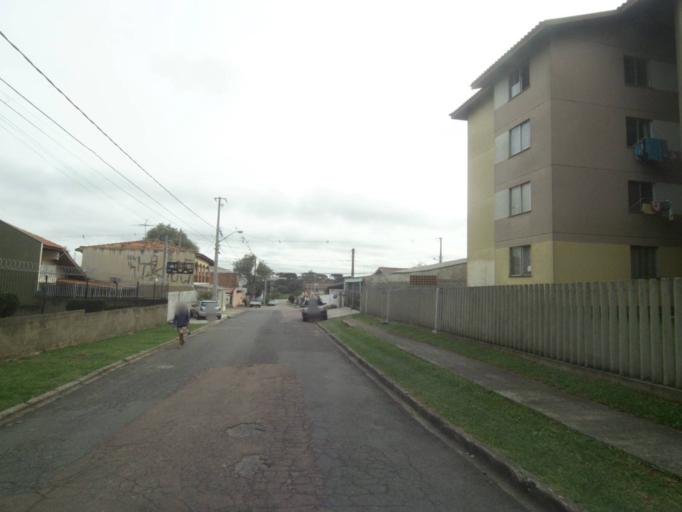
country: BR
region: Parana
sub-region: Sao Jose Dos Pinhais
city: Sao Jose dos Pinhais
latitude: -25.5520
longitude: -49.2660
